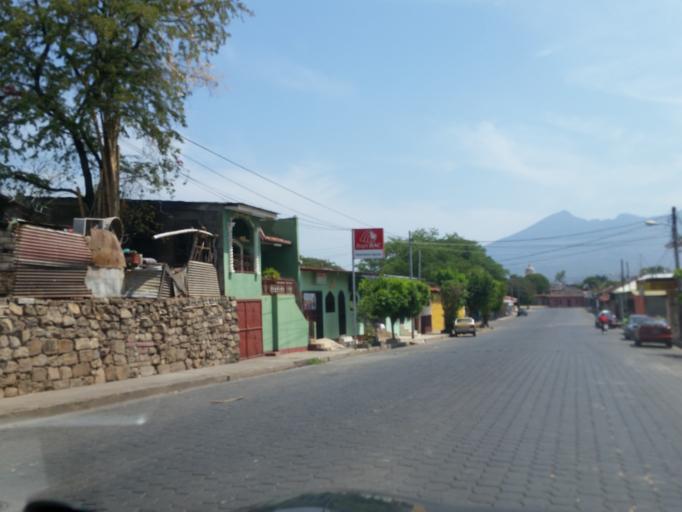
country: NI
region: Granada
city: Granada
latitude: 11.9353
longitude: -85.9572
